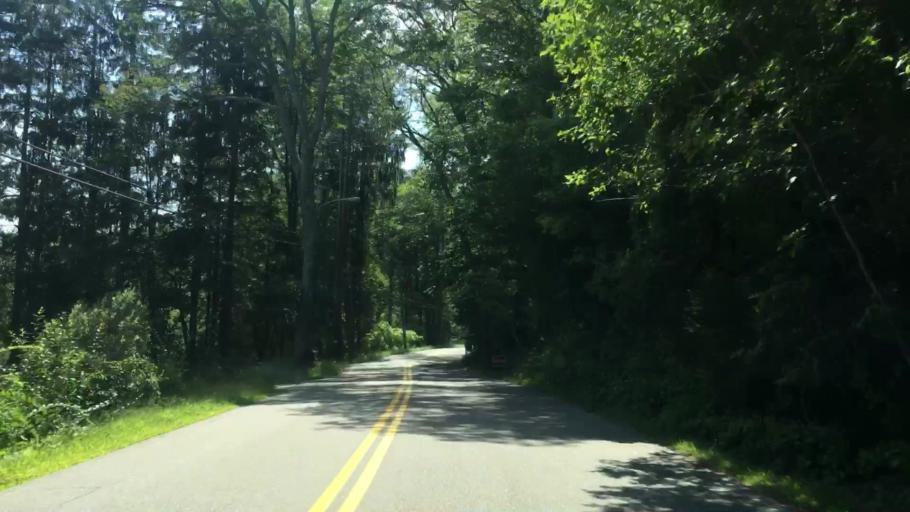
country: US
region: Maine
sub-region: Cumberland County
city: South Portland
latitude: 43.6101
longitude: -70.2658
